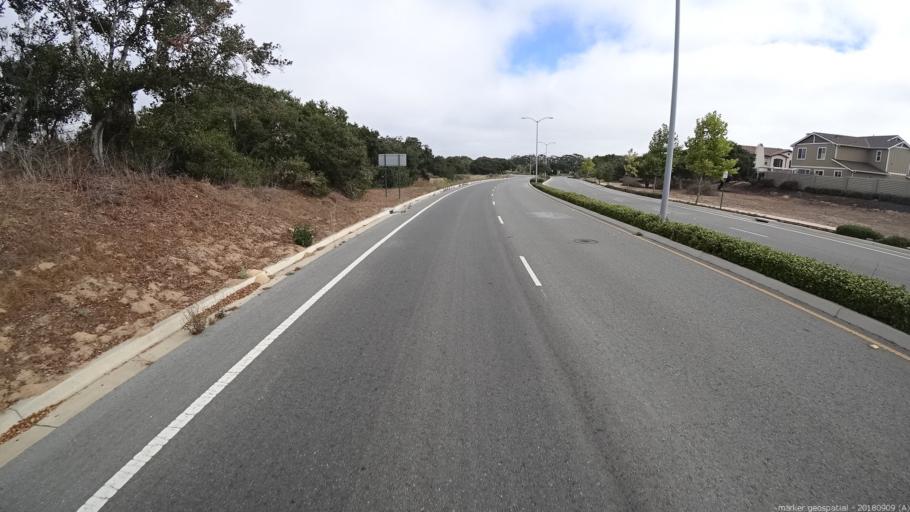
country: US
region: California
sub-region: Monterey County
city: Marina
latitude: 36.6564
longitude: -121.7435
